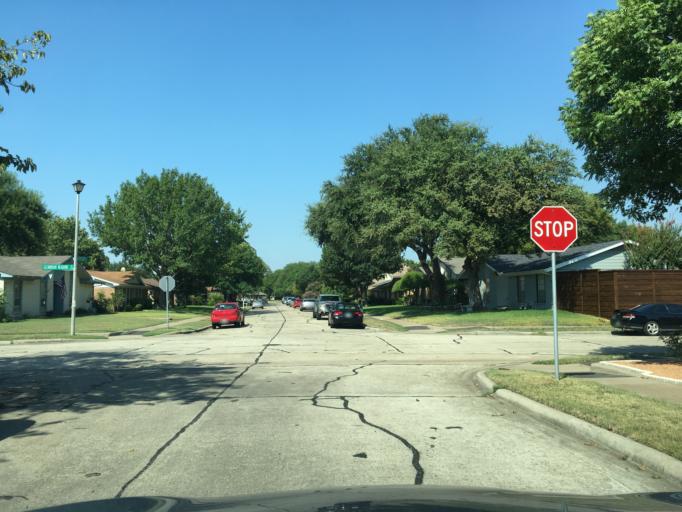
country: US
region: Texas
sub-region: Dallas County
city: Garland
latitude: 32.9343
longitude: -96.6363
